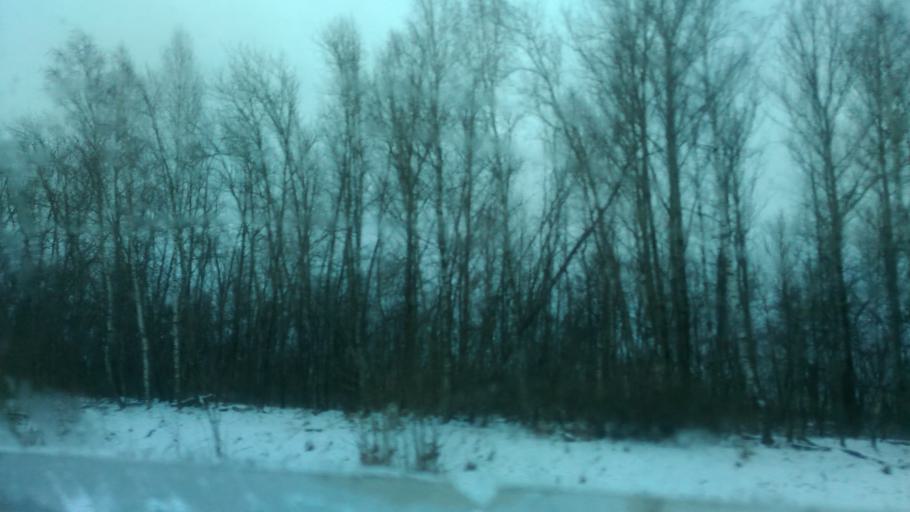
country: RU
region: Tula
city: Bolokhovo
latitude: 54.0730
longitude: 37.7918
